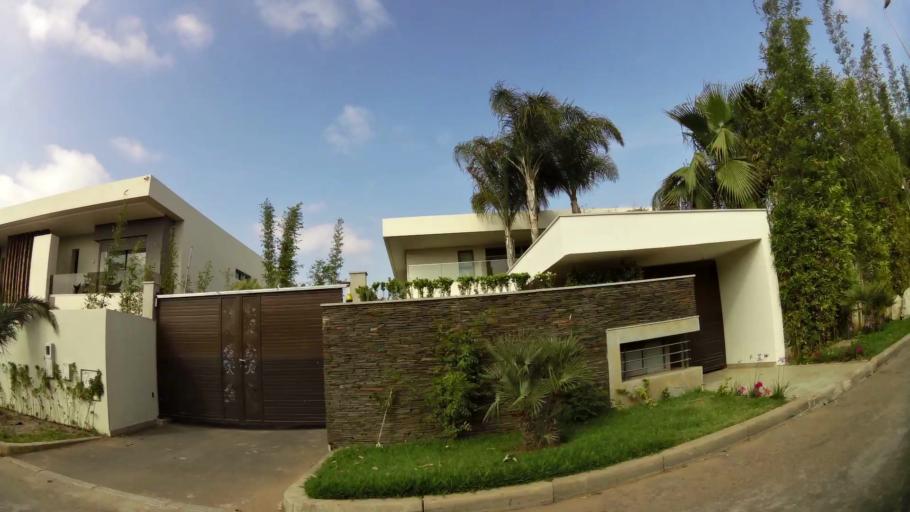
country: MA
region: Rabat-Sale-Zemmour-Zaer
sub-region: Rabat
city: Rabat
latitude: 33.9610
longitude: -6.8394
